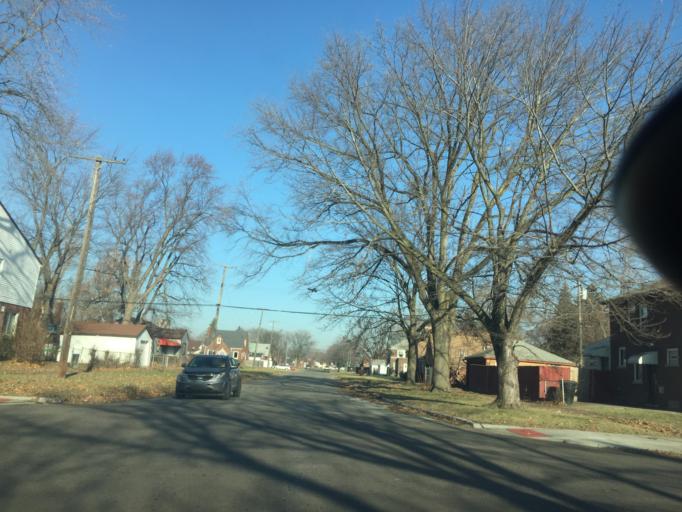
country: US
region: Michigan
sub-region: Macomb County
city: Eastpointe
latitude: 42.4473
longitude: -82.9561
